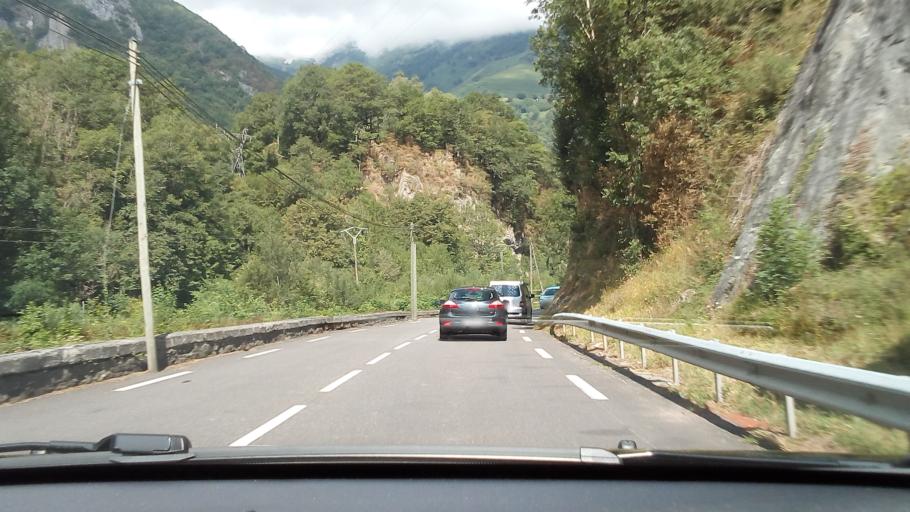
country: FR
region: Aquitaine
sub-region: Departement des Pyrenees-Atlantiques
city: Laruns
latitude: 42.9428
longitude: -0.6072
